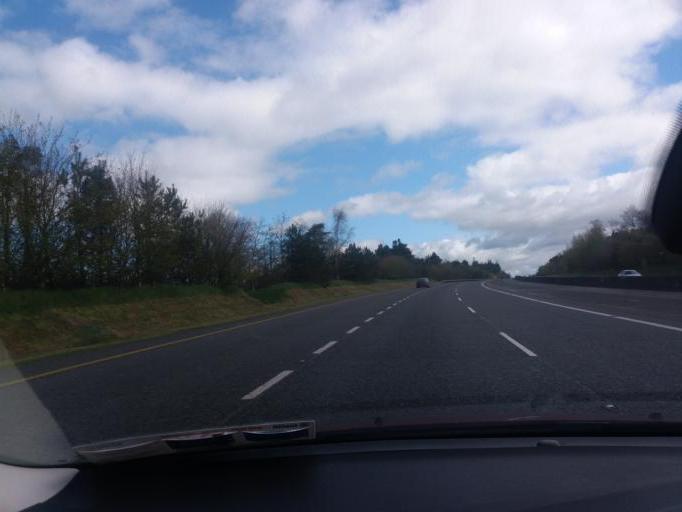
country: IE
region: Munster
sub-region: County Cork
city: Fermoy
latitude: 52.1197
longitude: -8.2703
